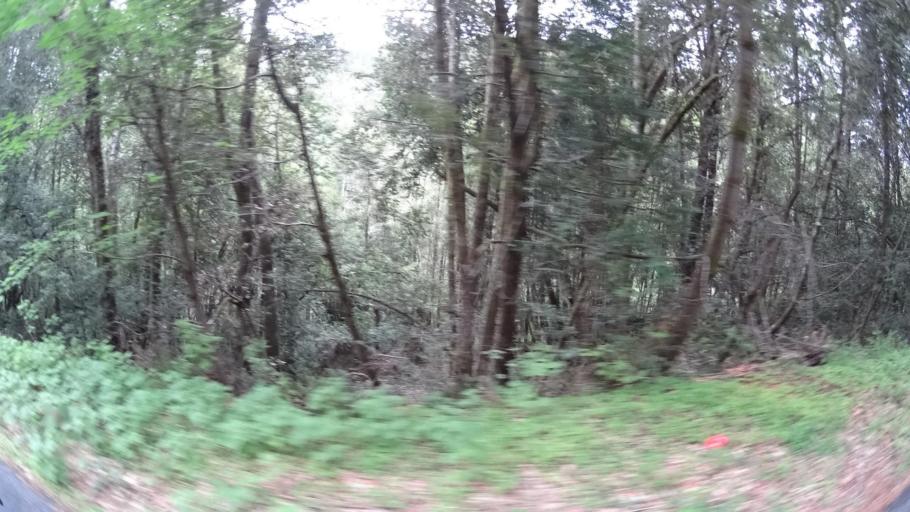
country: US
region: California
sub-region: Humboldt County
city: Blue Lake
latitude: 40.9572
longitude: -123.8376
